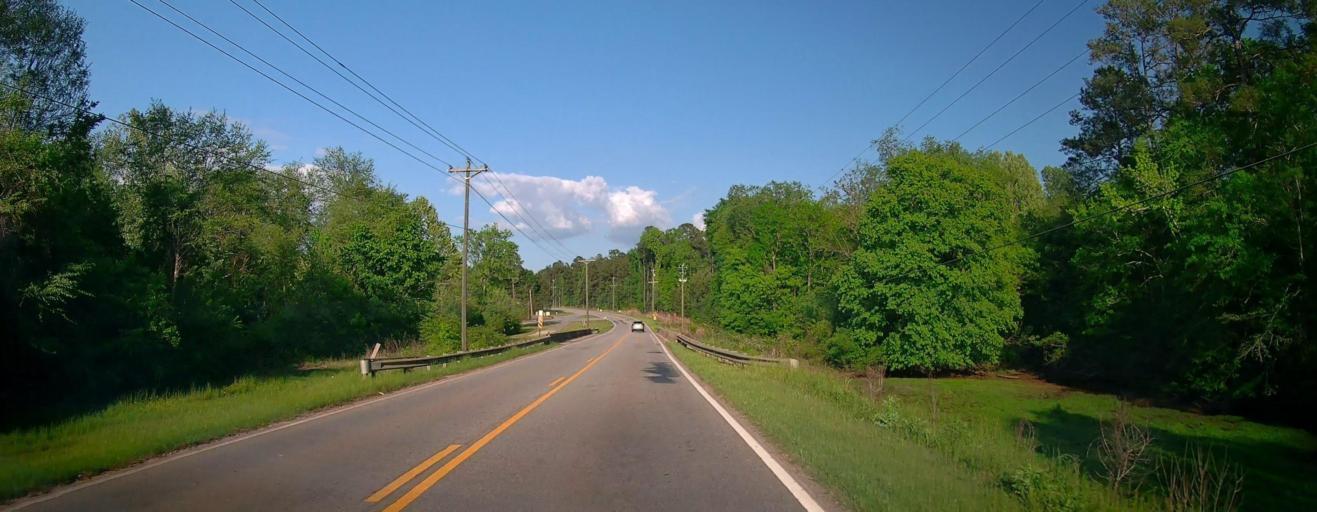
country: US
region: Georgia
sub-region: Putnam County
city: Eatonton
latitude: 33.2382
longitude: -83.3141
